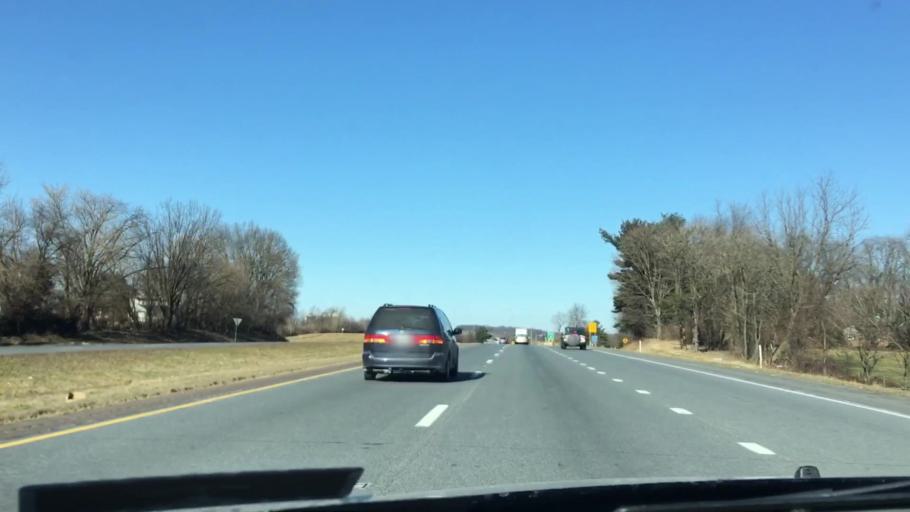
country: US
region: Pennsylvania
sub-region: Lancaster County
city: Brownstown
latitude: 40.0986
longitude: -76.2584
